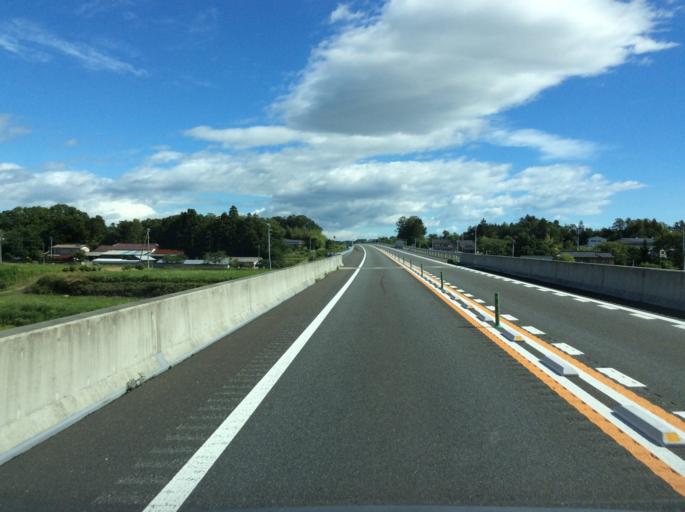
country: JP
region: Fukushima
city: Namie
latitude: 37.5606
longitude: 140.9455
